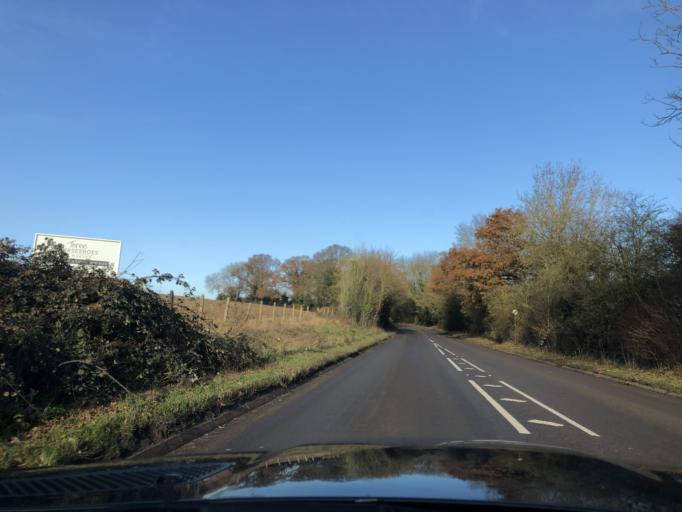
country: GB
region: England
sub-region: Buckinghamshire
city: Marlow
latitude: 51.5912
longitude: -0.7669
